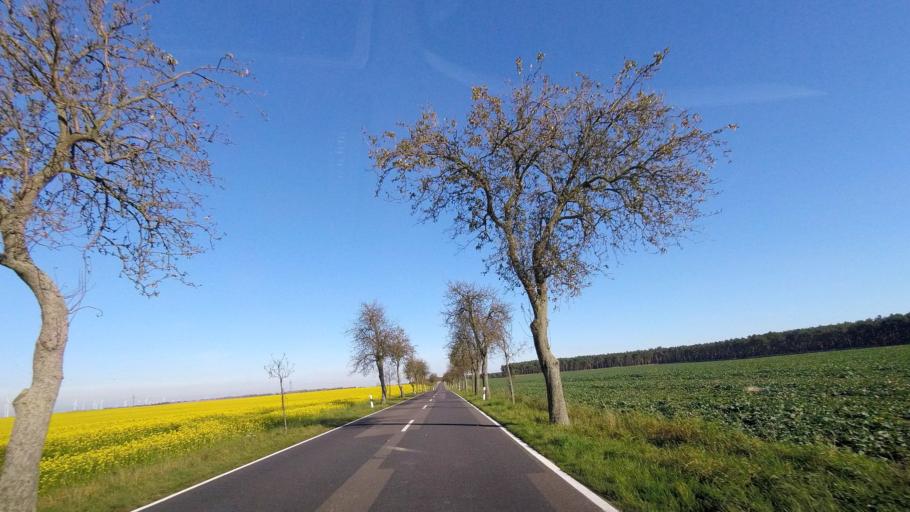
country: DE
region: Saxony-Anhalt
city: Kropstadt
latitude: 51.9727
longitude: 12.8049
